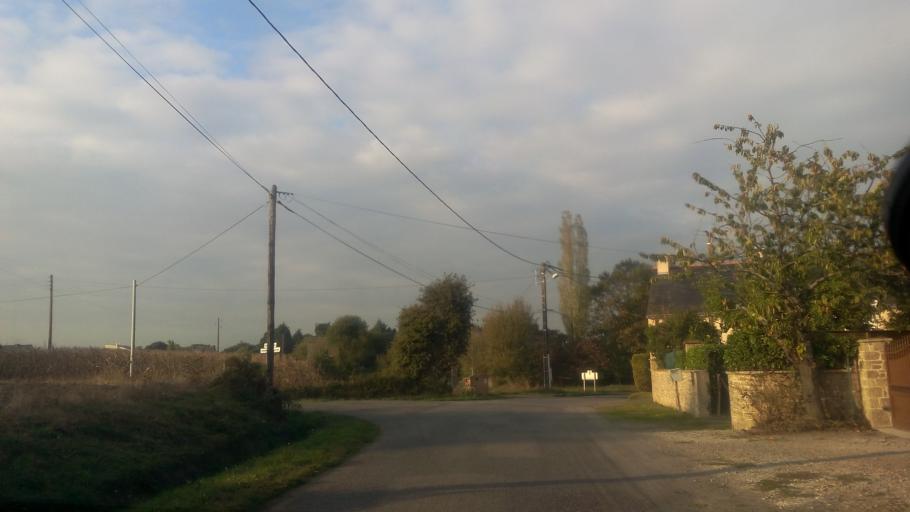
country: FR
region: Brittany
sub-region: Departement du Morbihan
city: Saint-Jean-la-Poterie
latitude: 47.6331
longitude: -2.1316
